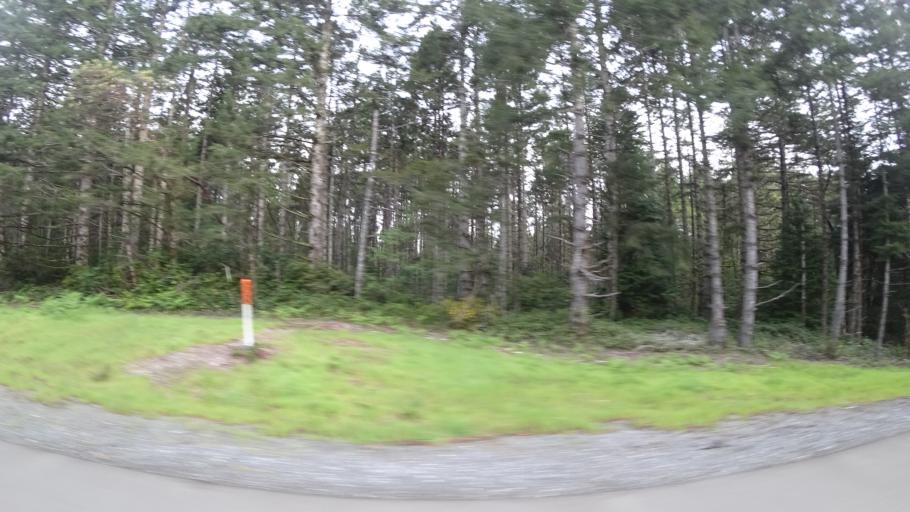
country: US
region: Oregon
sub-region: Coos County
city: Bandon
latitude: 43.1776
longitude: -124.3674
